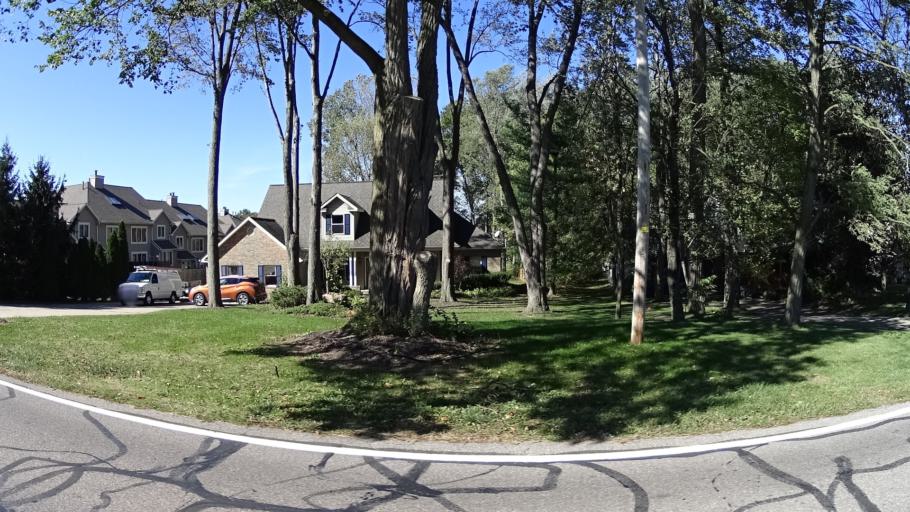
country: US
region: Ohio
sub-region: Lorain County
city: Amherst
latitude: 41.3846
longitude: -82.2206
